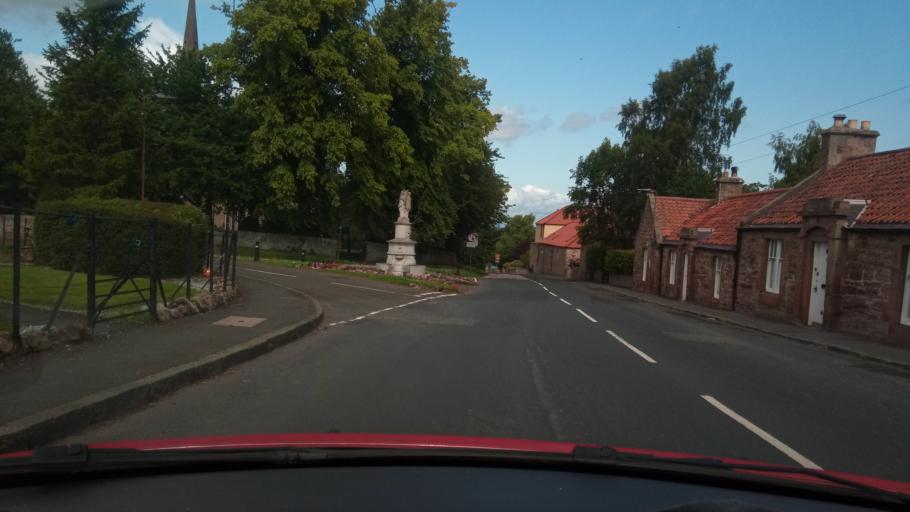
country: GB
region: Scotland
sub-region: East Lothian
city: Pencaitland
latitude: 55.9008
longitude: -2.8409
